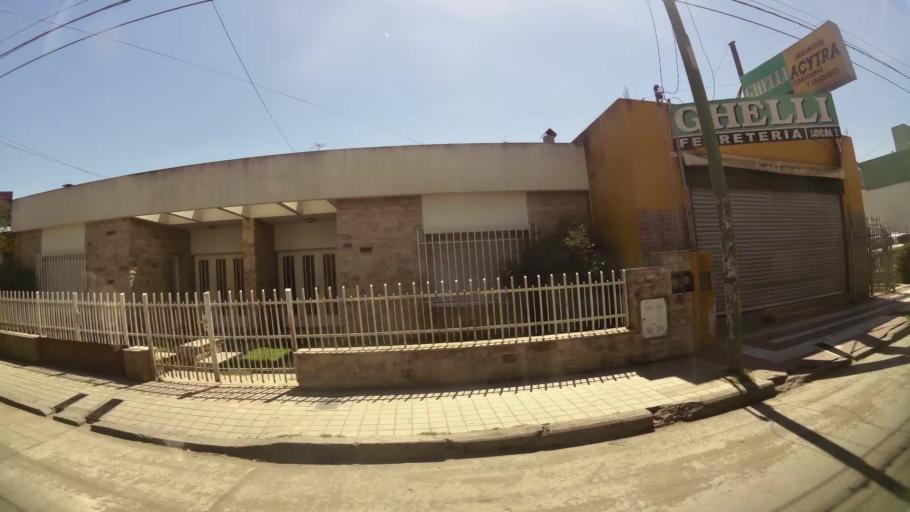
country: AR
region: Cordoba
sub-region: Departamento de Capital
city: Cordoba
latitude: -31.3785
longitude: -64.1479
